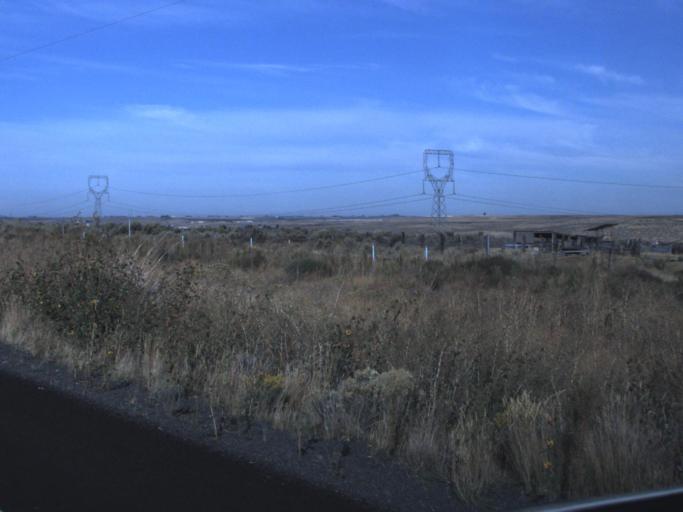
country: US
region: Washington
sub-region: Franklin County
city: Connell
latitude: 46.6347
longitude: -118.7700
